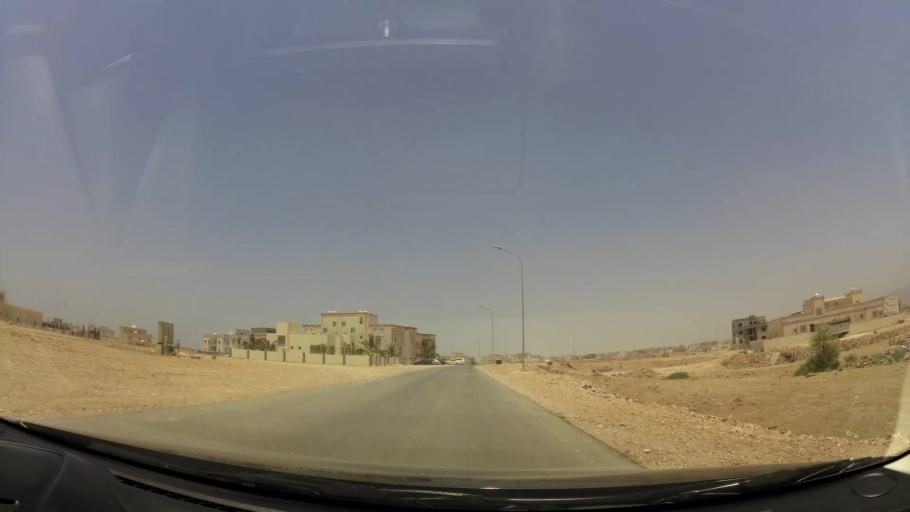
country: OM
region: Zufar
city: Salalah
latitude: 17.0968
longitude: 54.1696
